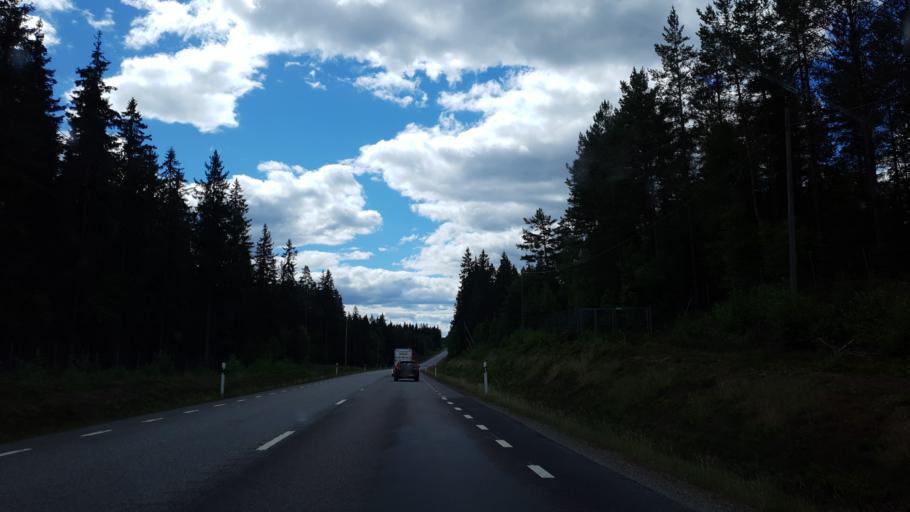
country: SE
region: Kronoberg
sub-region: Vaxjo Kommun
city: Braas
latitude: 57.1771
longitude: 15.1596
